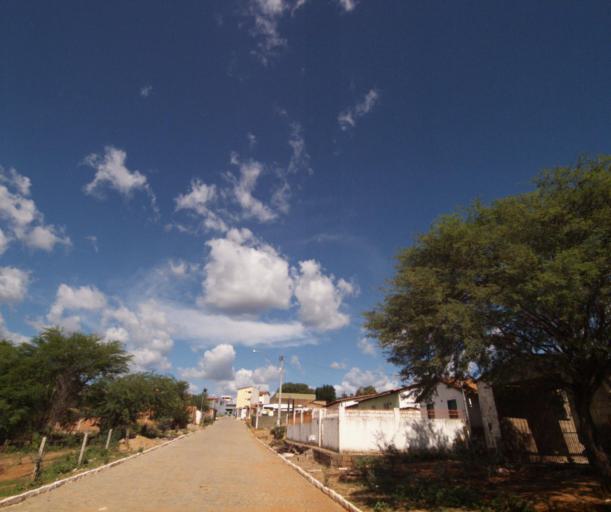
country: BR
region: Bahia
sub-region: Pocoes
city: Pocoes
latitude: -14.2417
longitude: -40.7749
